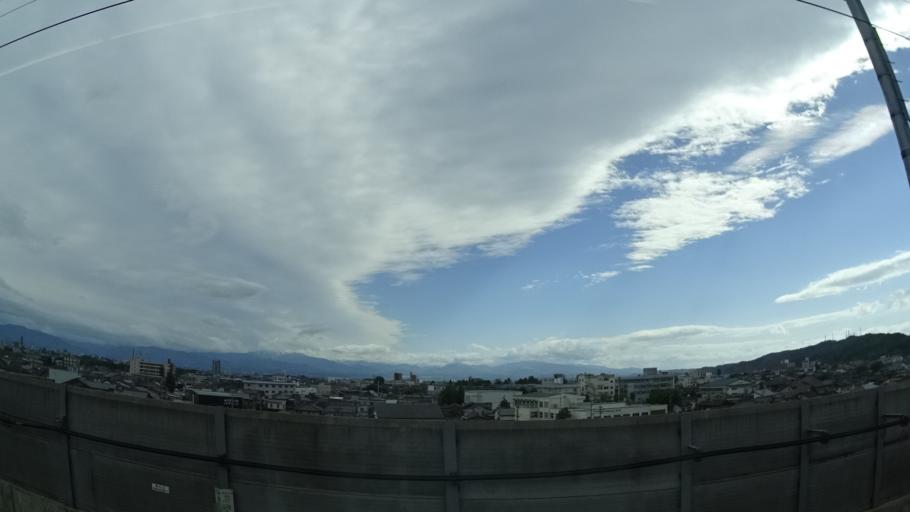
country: JP
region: Toyama
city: Toyama-shi
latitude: 36.7084
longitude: 137.1972
